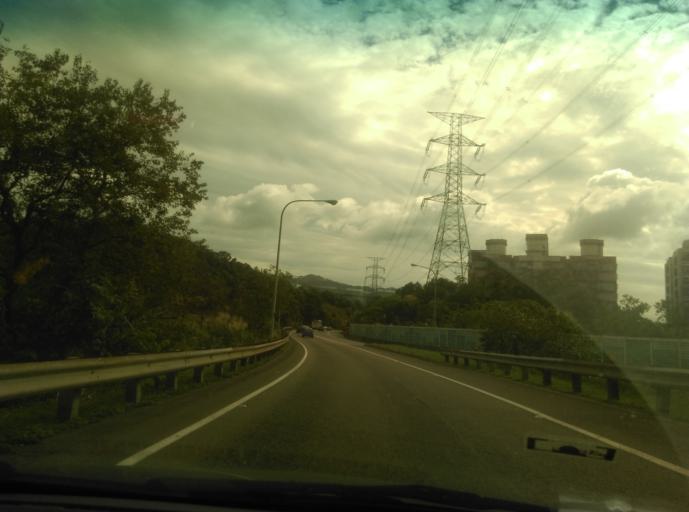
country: TW
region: Taipei
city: Taipei
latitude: 25.0711
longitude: 121.6433
